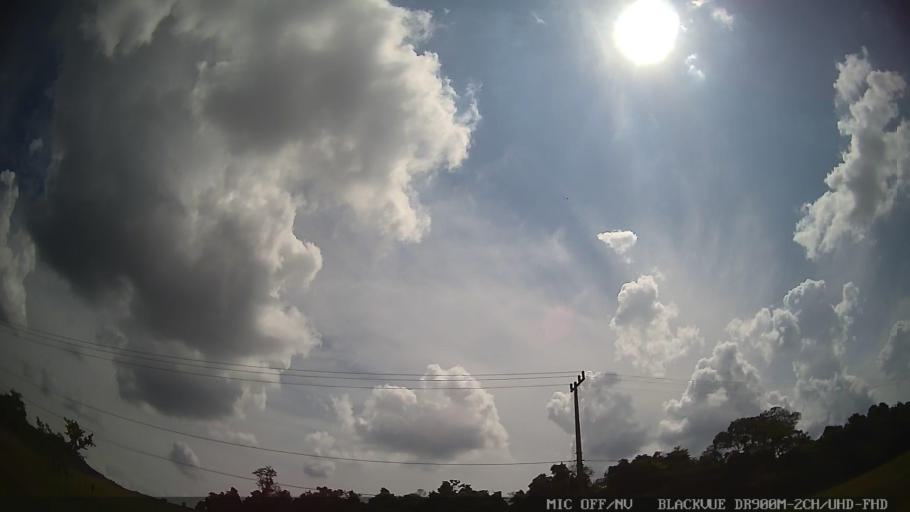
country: BR
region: Sao Paulo
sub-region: Braganca Paulista
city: Braganca Paulista
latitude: -22.9533
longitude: -46.6159
